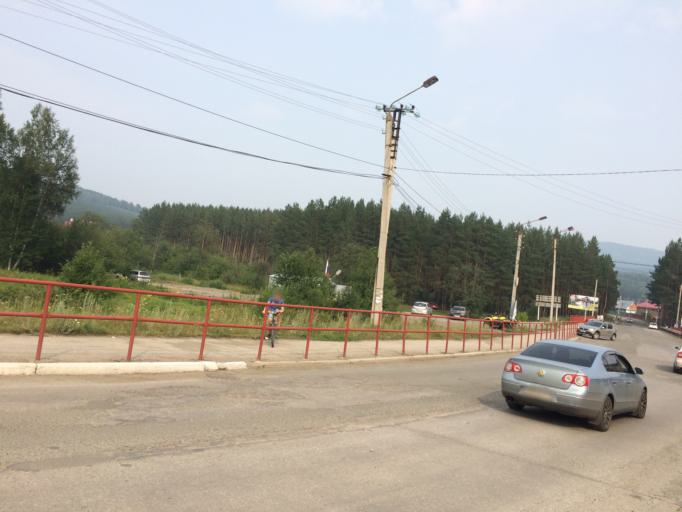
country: RU
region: Bashkortostan
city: Abzakovo
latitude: 53.8111
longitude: 58.6364
